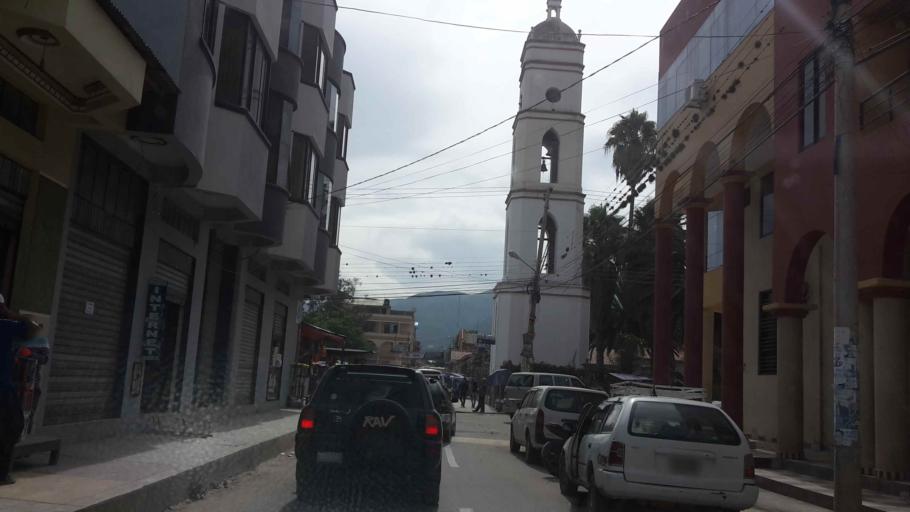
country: BO
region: Cochabamba
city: Cochabamba
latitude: -17.3378
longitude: -66.2648
